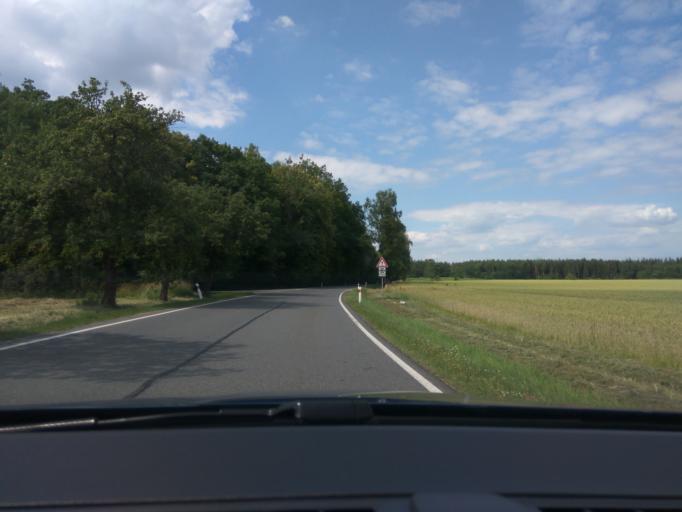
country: CZ
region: Jihocesky
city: Milevsko
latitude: 49.4168
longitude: 14.3581
